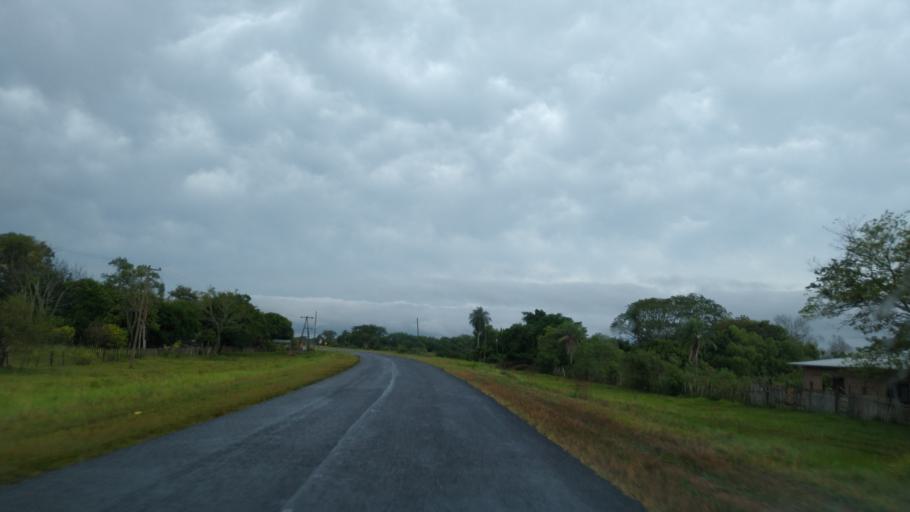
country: AR
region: Corrientes
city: Loreto
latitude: -27.7729
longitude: -57.2691
